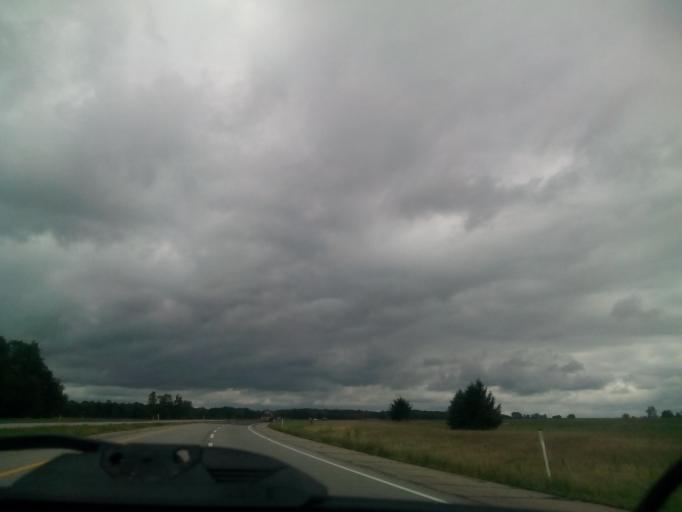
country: US
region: Michigan
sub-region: Branch County
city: Bronson
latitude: 41.7533
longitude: -85.2662
